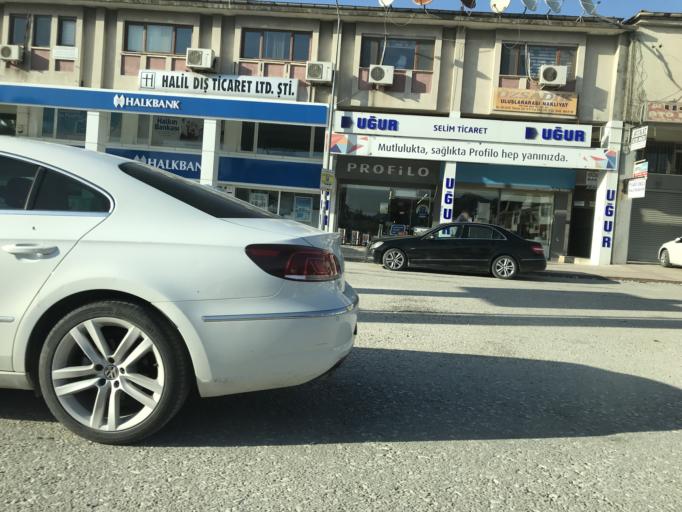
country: TR
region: Hatay
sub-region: Antakya Ilcesi
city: Antakya
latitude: 36.2082
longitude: 36.1678
